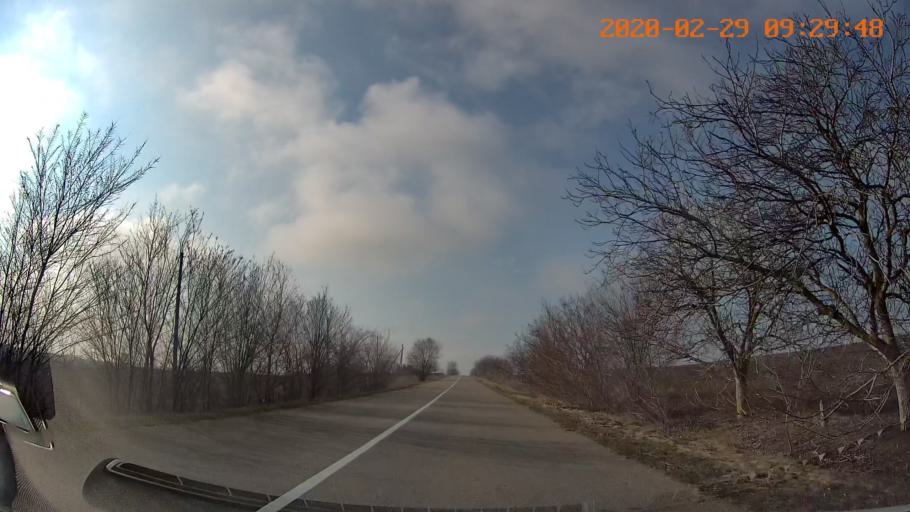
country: UA
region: Odessa
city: Lymanske
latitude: 46.6741
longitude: 29.9194
